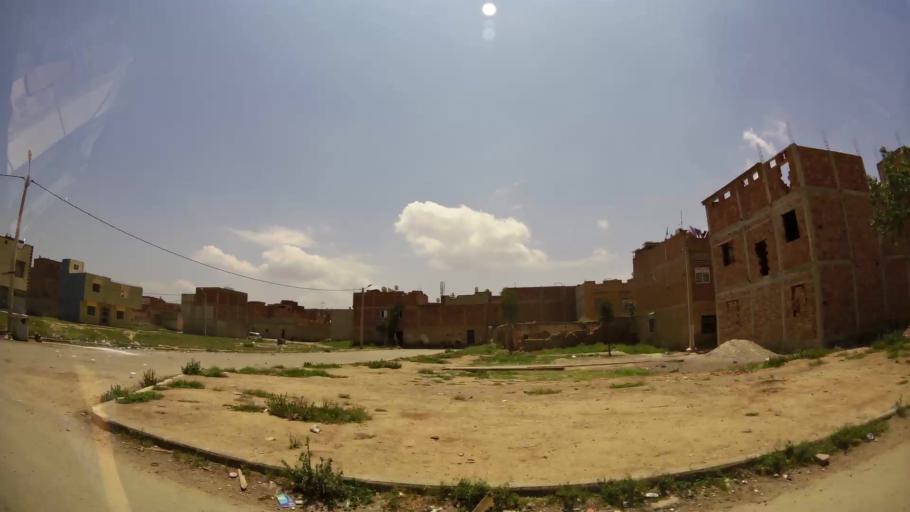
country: MA
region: Oriental
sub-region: Oujda-Angad
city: Oujda
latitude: 34.6816
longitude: -1.8972
